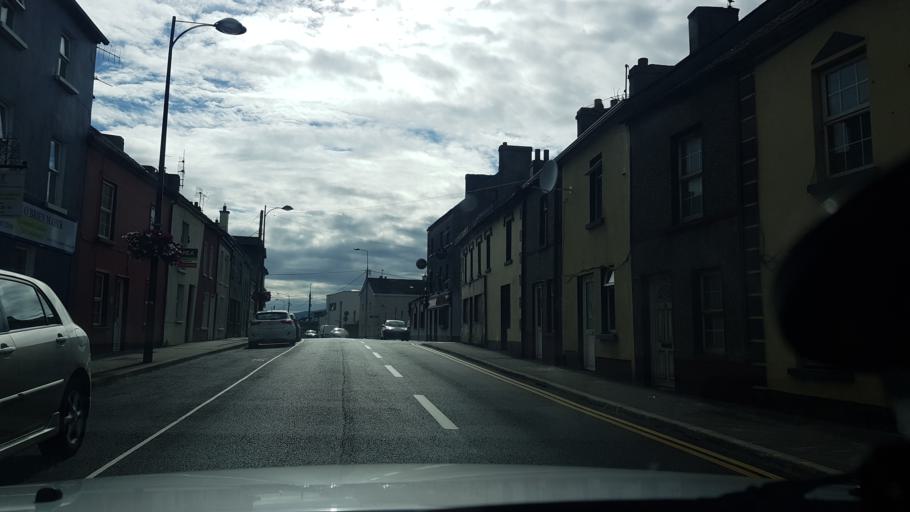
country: IE
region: Munster
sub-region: North Tipperary
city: Nenagh
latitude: 52.8634
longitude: -8.2037
